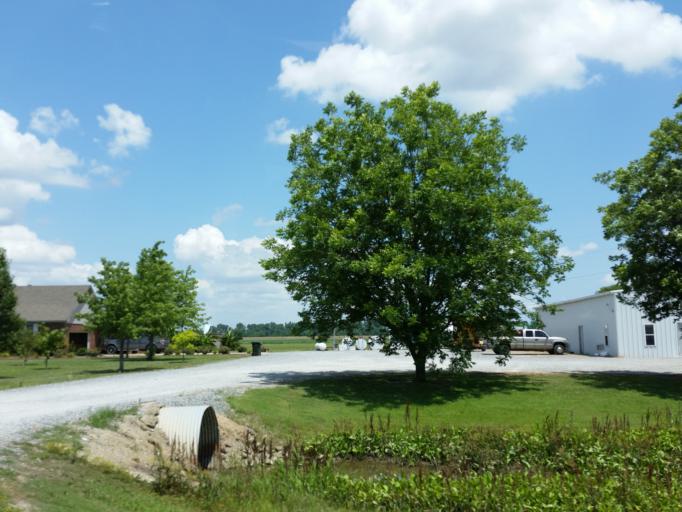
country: US
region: Kentucky
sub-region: Fulton County
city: Hickman
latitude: 36.5471
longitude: -89.2597
